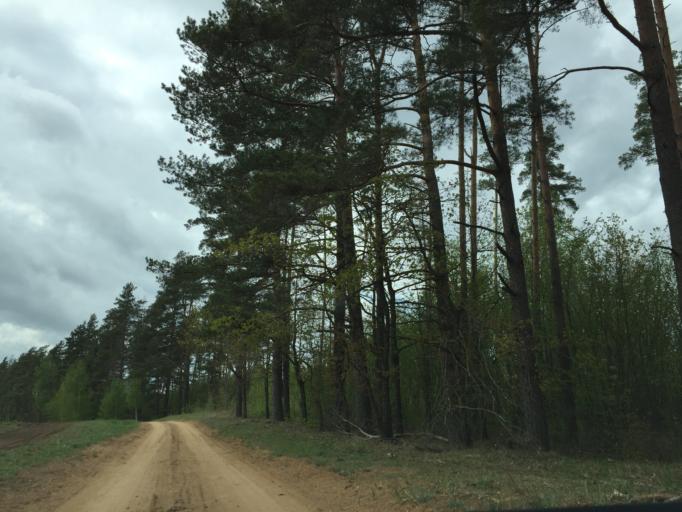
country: LV
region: Kekava
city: Kekava
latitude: 56.8002
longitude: 24.3048
